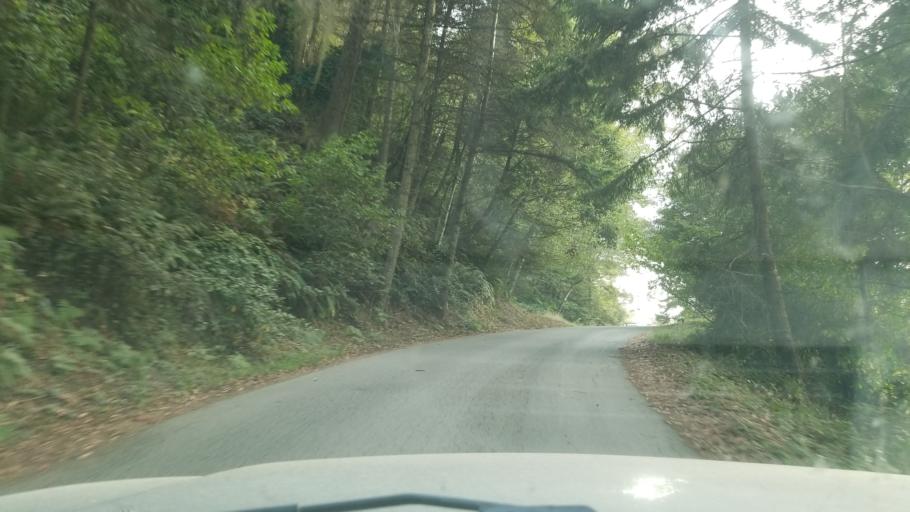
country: US
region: California
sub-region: Mendocino County
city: Fort Bragg
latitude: 39.4292
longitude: -123.7950
